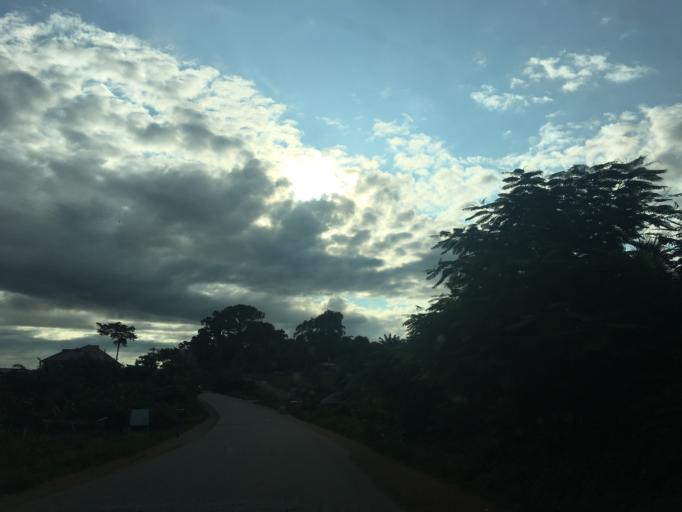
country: GH
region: Western
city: Bibiani
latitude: 6.3305
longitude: -2.2535
